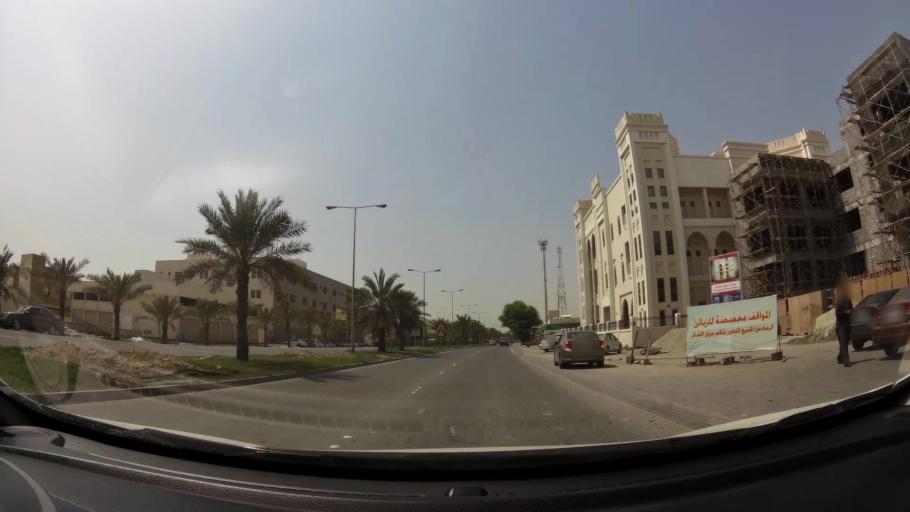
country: BH
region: Manama
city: Jidd Hafs
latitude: 26.2153
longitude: 50.4667
